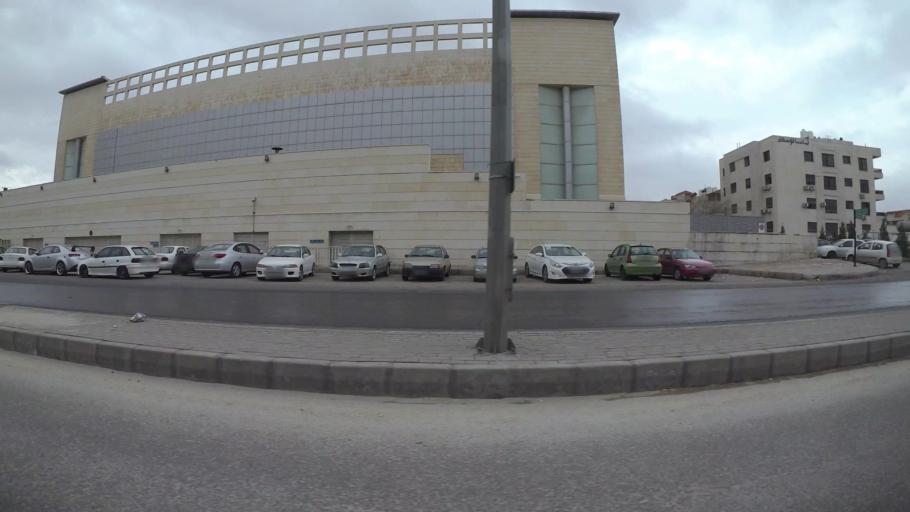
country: JO
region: Amman
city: Wadi as Sir
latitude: 31.9813
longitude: 35.8392
